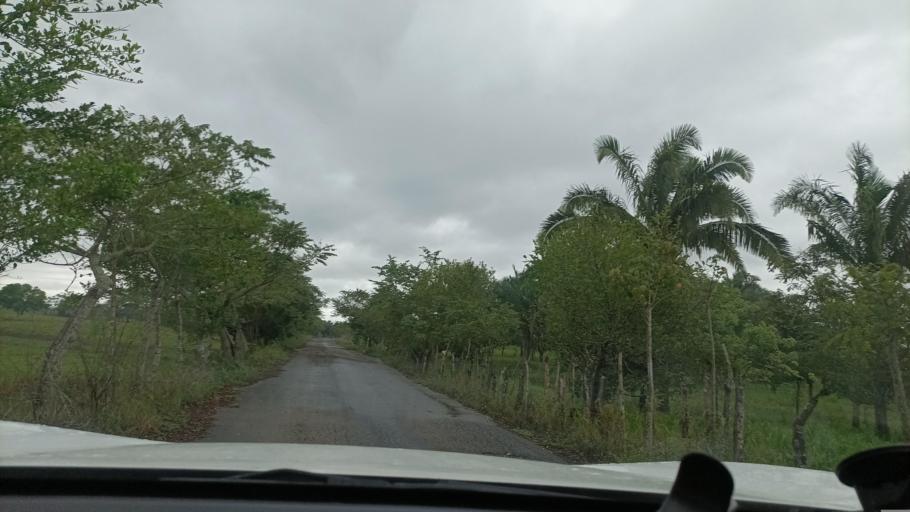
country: MX
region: Veracruz
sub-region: Moloacan
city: Cuichapa
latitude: 17.7718
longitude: -94.3881
